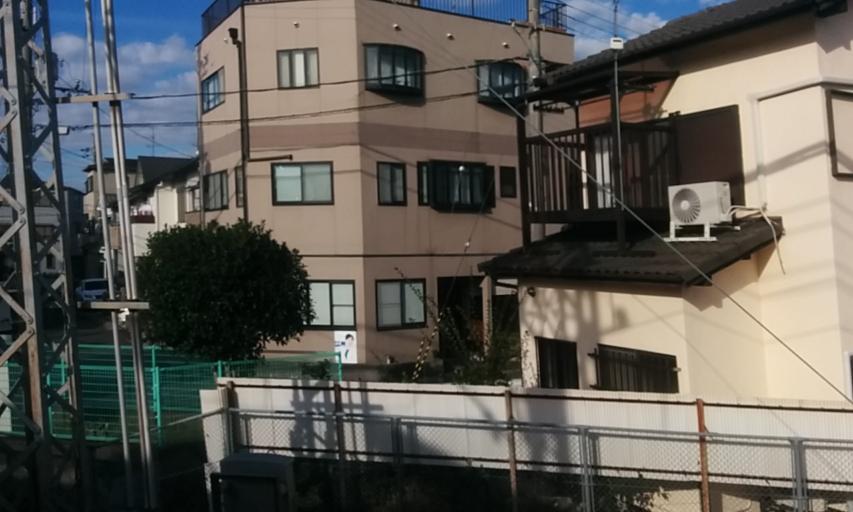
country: JP
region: Kyoto
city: Uji
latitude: 34.8911
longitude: 135.7813
